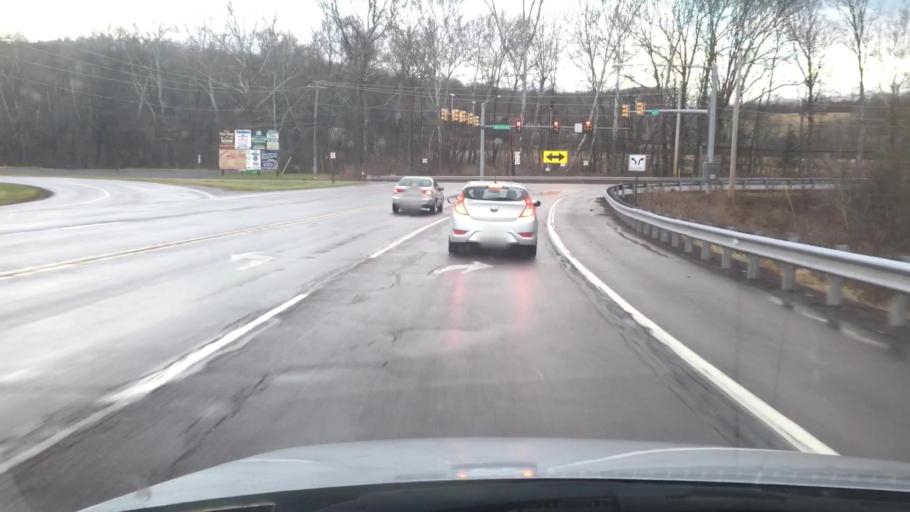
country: US
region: Pennsylvania
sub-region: Columbia County
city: Bloomsburg
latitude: 41.0267
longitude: -76.4811
